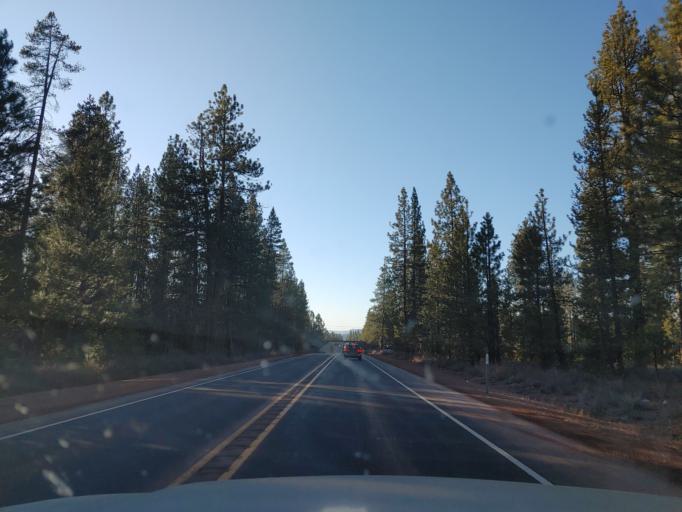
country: US
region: Oregon
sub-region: Deschutes County
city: La Pine
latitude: 43.3754
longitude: -121.7961
